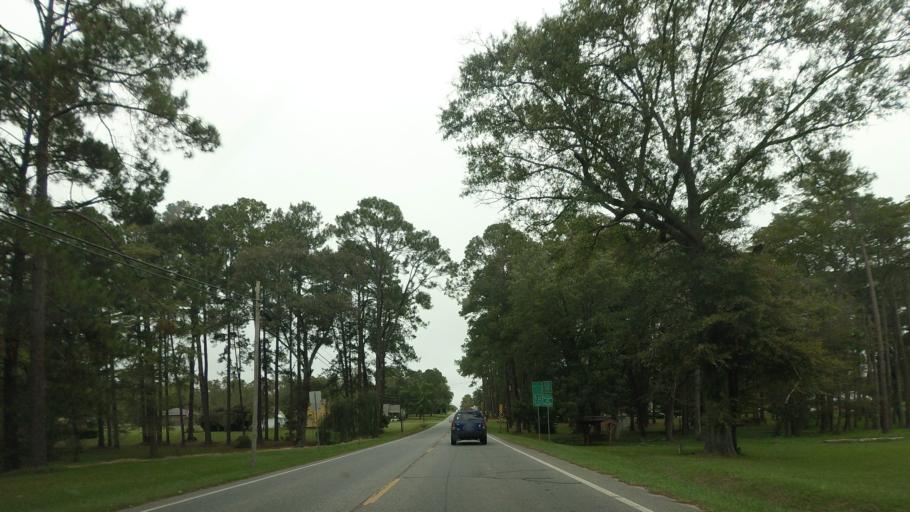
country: US
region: Georgia
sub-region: Irwin County
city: Ocilla
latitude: 31.5879
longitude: -83.2507
